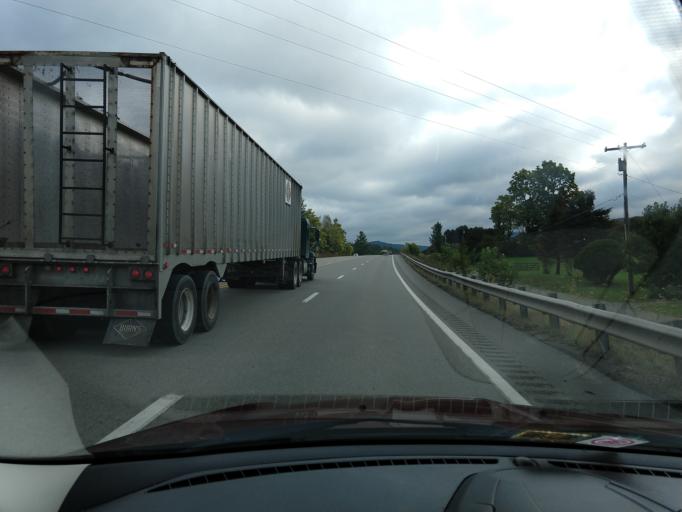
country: US
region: West Virginia
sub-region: Randolph County
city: Elkins
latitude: 38.8639
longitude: -79.8544
